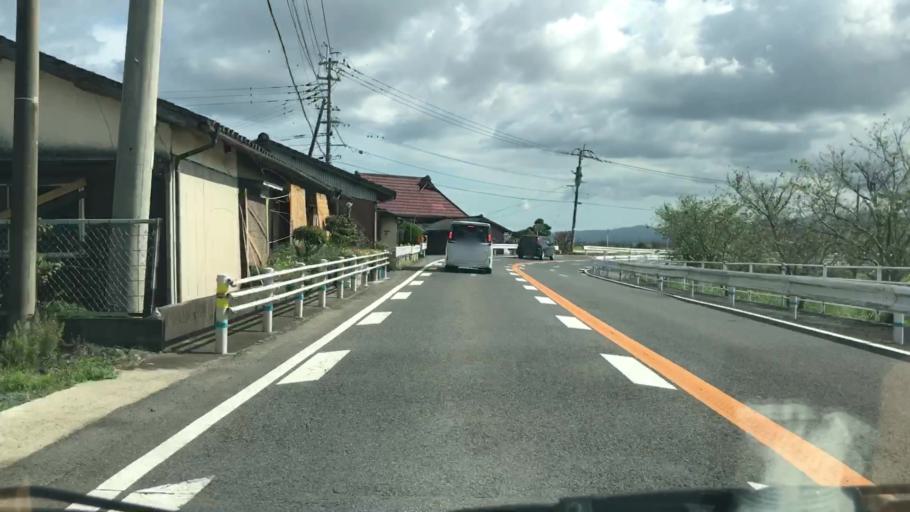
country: JP
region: Saga Prefecture
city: Kashima
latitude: 33.1636
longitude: 130.1682
